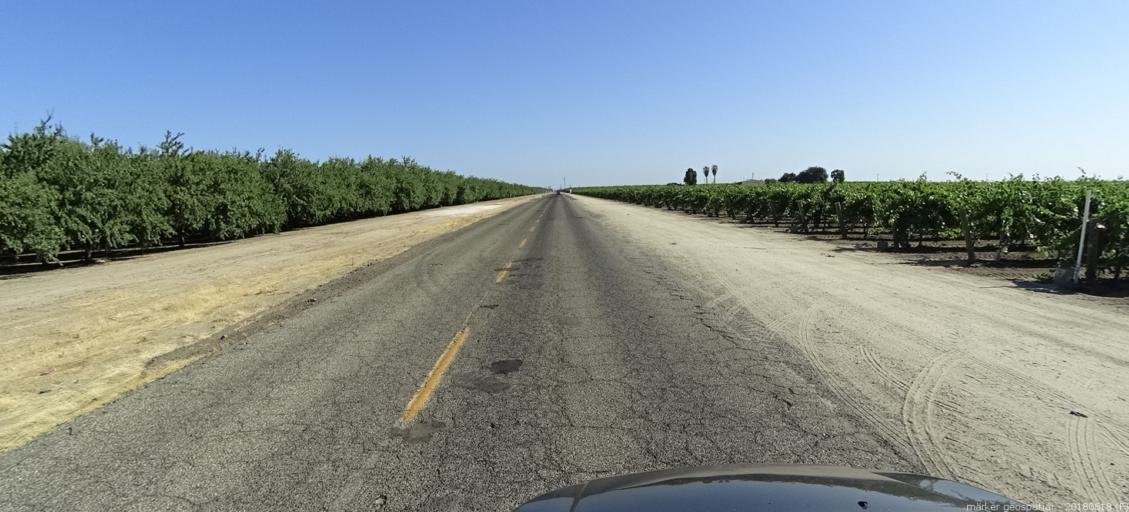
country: US
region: California
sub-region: Madera County
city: Parkwood
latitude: 36.8983
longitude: -120.1286
